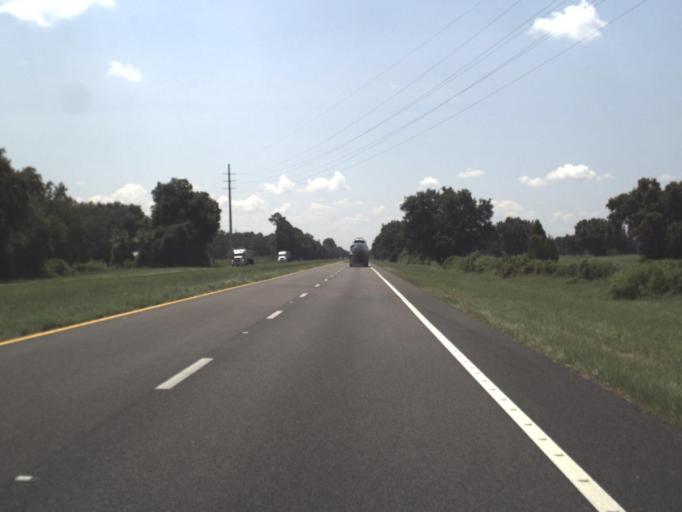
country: US
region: Florida
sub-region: Levy County
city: Inglis
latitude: 28.9954
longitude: -82.6520
